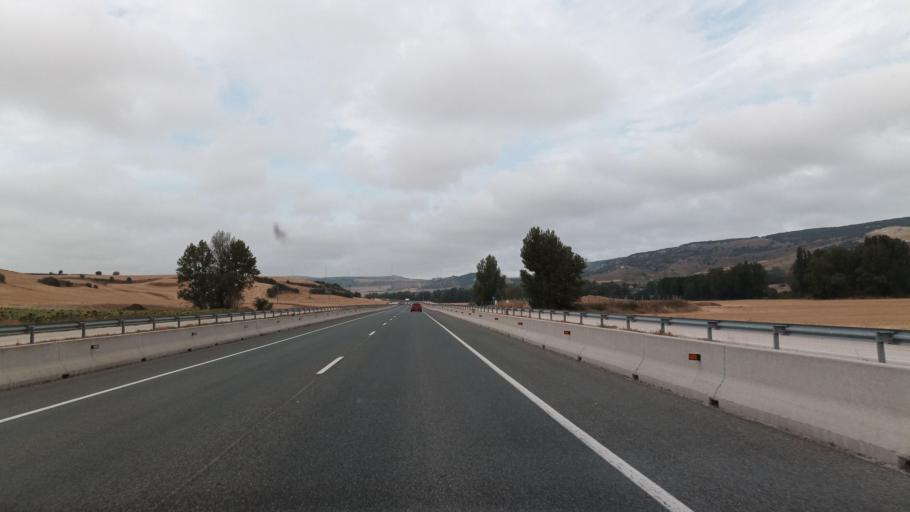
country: ES
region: Castille and Leon
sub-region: Provincia de Burgos
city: Castil de Peones
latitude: 42.4794
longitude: -3.4041
